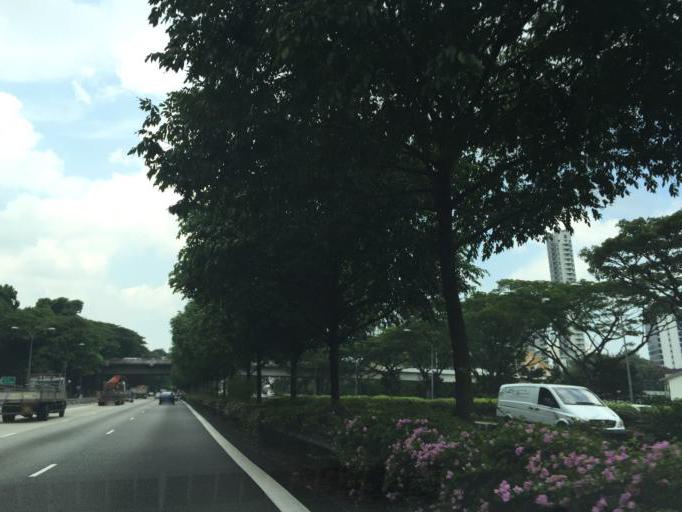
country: SG
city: Singapore
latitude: 1.3298
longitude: 103.8446
